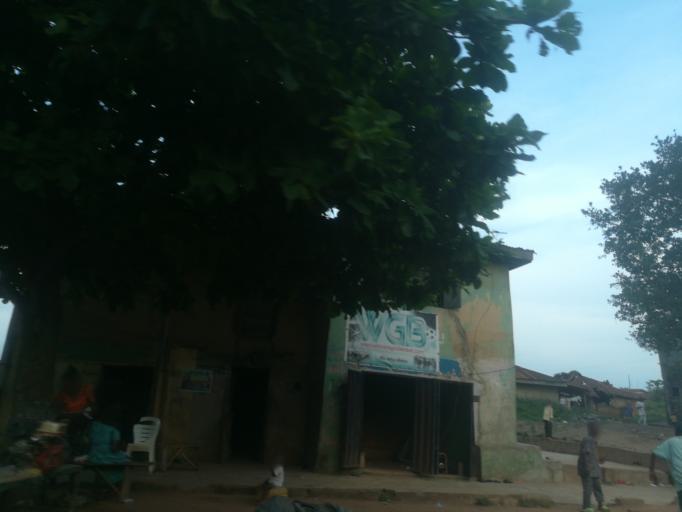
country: NG
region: Oyo
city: Moniya
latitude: 7.5286
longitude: 3.9088
